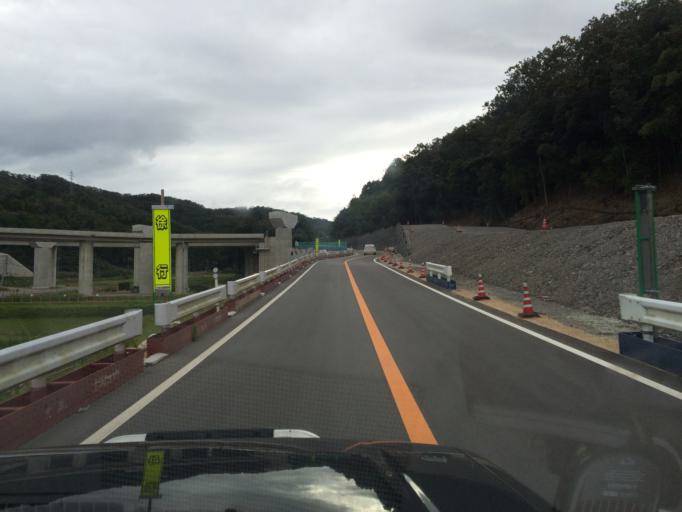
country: JP
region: Hyogo
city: Toyooka
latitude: 35.5080
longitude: 134.8044
